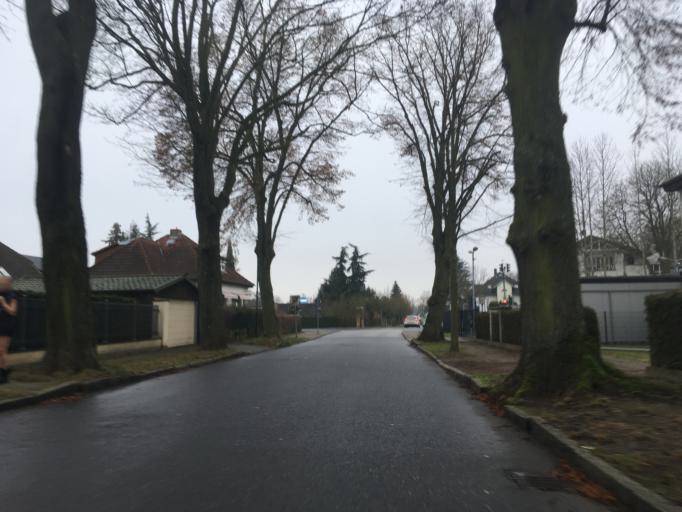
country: DE
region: Berlin
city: Buch
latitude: 52.6319
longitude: 13.5196
